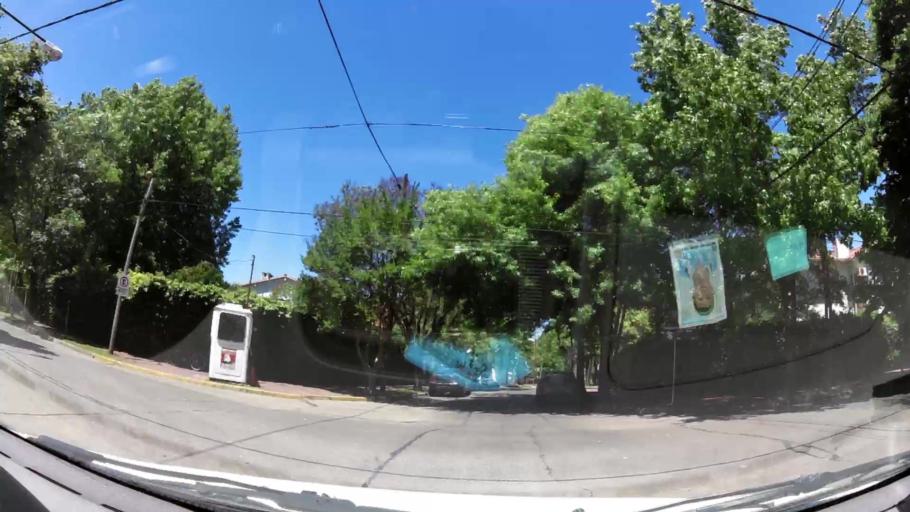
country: AR
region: Buenos Aires
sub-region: Partido de San Isidro
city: San Isidro
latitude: -34.4770
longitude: -58.5050
